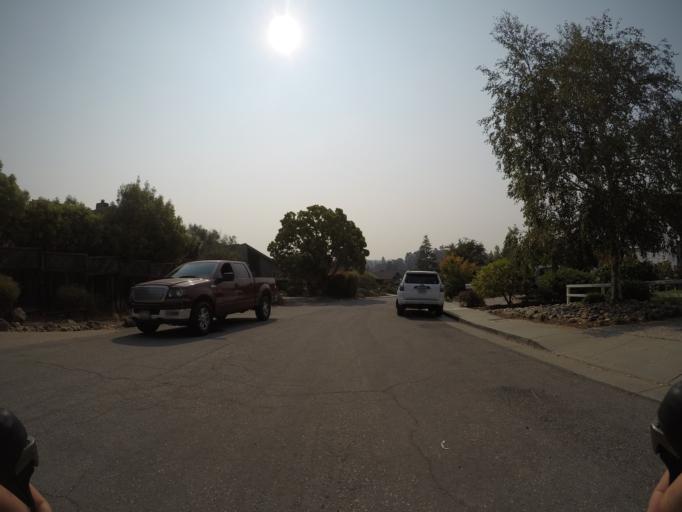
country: US
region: California
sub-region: Santa Cruz County
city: Live Oak
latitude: 36.9922
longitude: -121.9884
